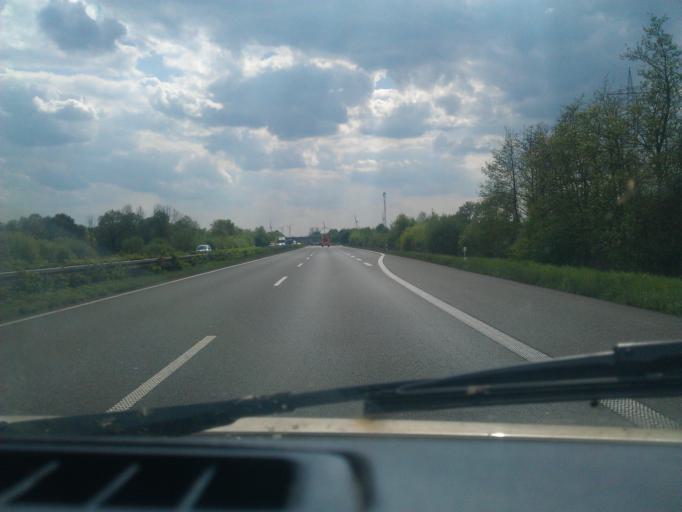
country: DE
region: North Rhine-Westphalia
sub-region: Regierungsbezirk Munster
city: Ochtrup
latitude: 52.2281
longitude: 7.1426
